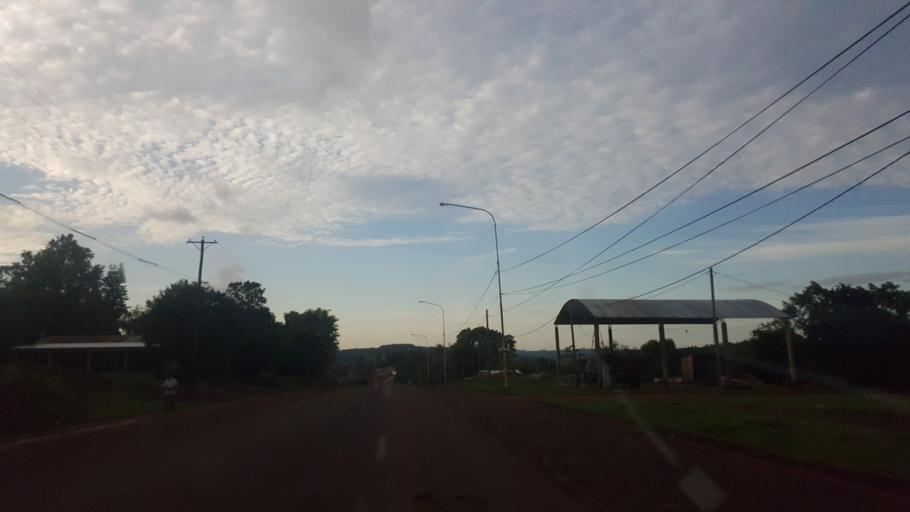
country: AR
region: Misiones
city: Dos de Mayo
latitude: -27.0316
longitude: -54.6859
